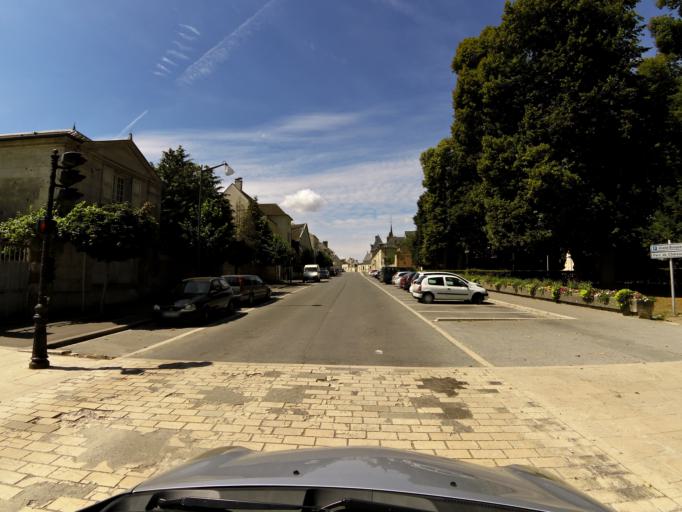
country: FR
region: Picardie
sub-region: Departement de l'Aisne
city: Villers-Cotterets
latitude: 49.2547
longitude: 3.0944
